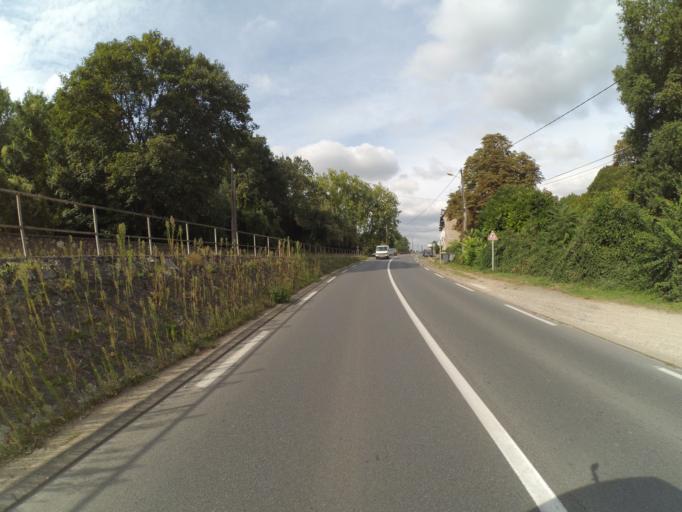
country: FR
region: Centre
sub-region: Departement d'Indre-et-Loire
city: Vouvray
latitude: 47.4066
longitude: 0.7995
